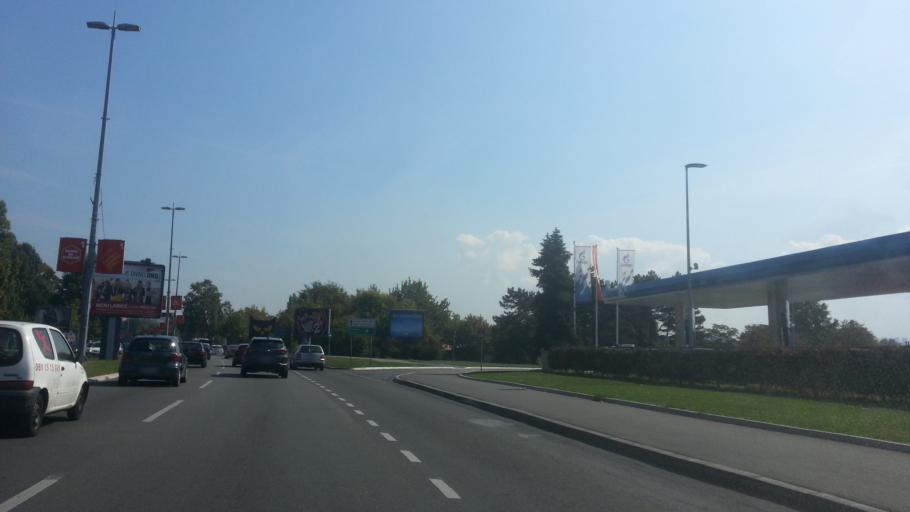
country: RS
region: Central Serbia
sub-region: Belgrade
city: Novi Beograd
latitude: 44.8144
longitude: 20.4362
